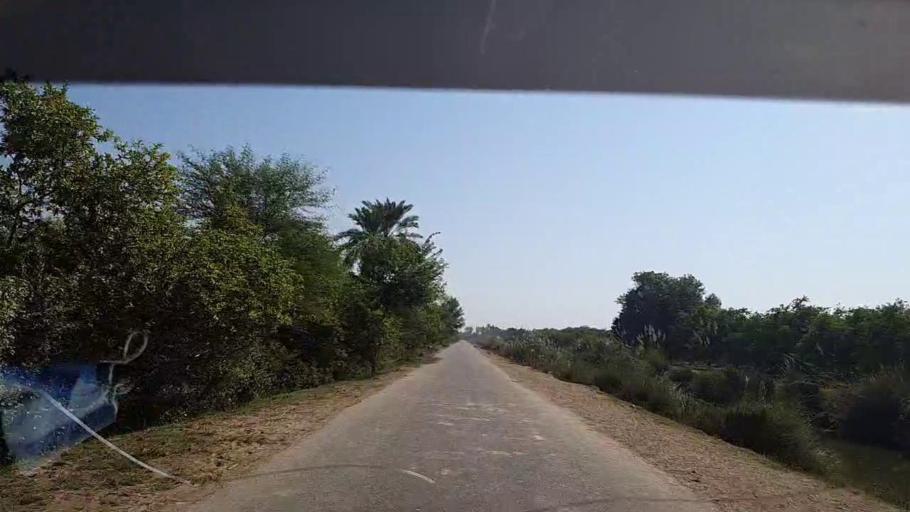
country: PK
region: Sindh
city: Larkana
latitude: 27.6039
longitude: 68.2617
